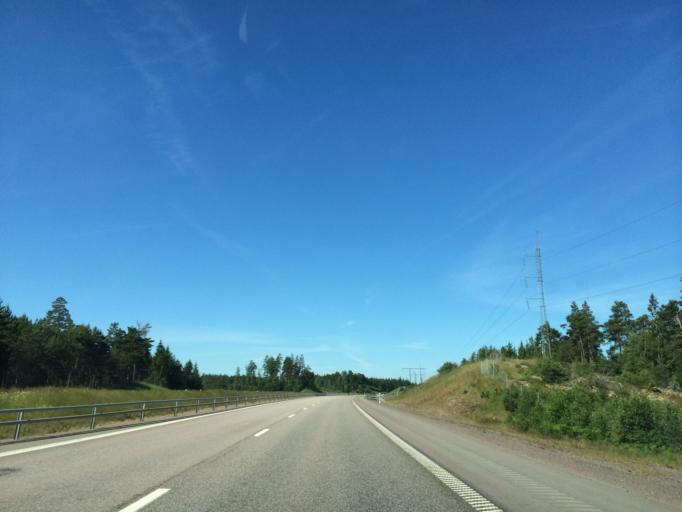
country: SE
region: OEstergoetland
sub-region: Vadstena Kommun
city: Herrestad
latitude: 58.2558
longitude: 14.8236
